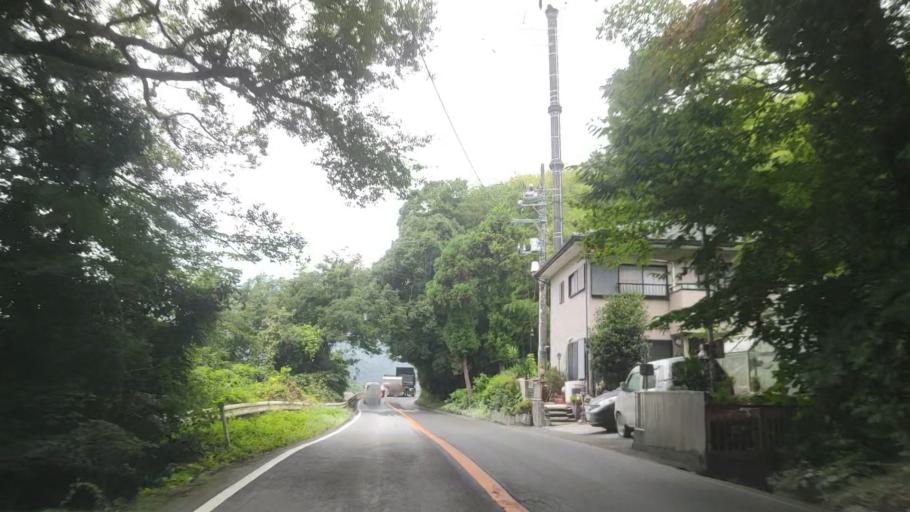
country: JP
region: Shizuoka
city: Fujinomiya
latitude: 35.2197
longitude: 138.5419
